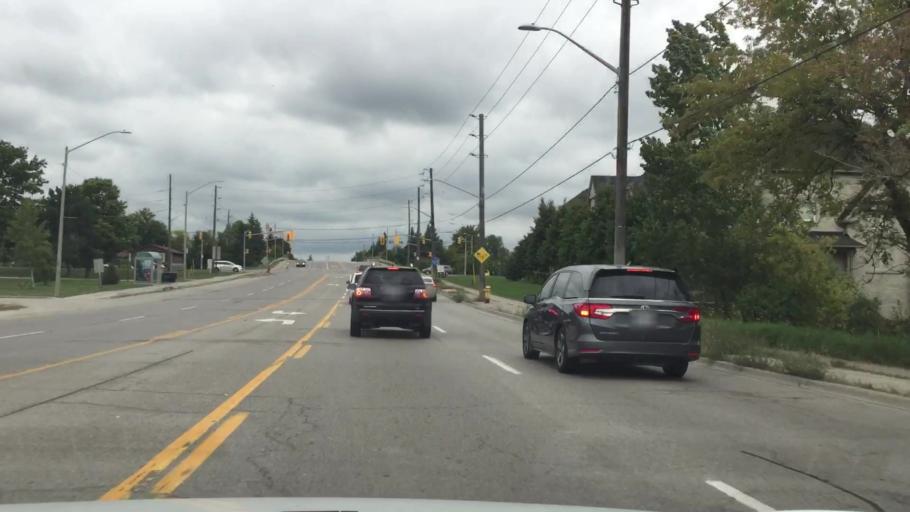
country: CA
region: Ontario
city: Pickering
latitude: 43.8209
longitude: -79.1163
